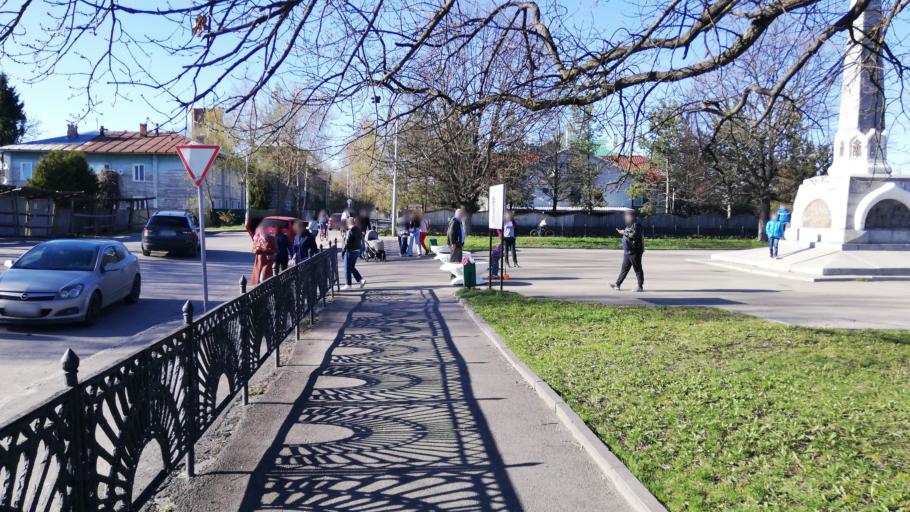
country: RU
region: Vologda
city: Vologda
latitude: 59.2289
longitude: 39.8747
